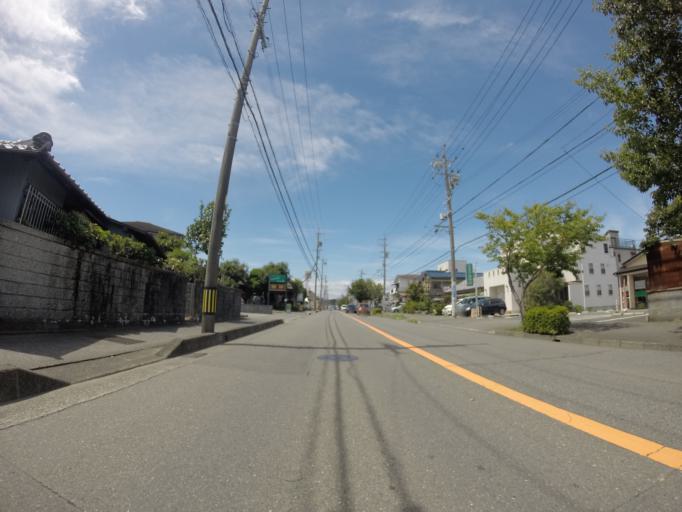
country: JP
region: Shizuoka
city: Shizuoka-shi
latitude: 34.9984
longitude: 138.4769
